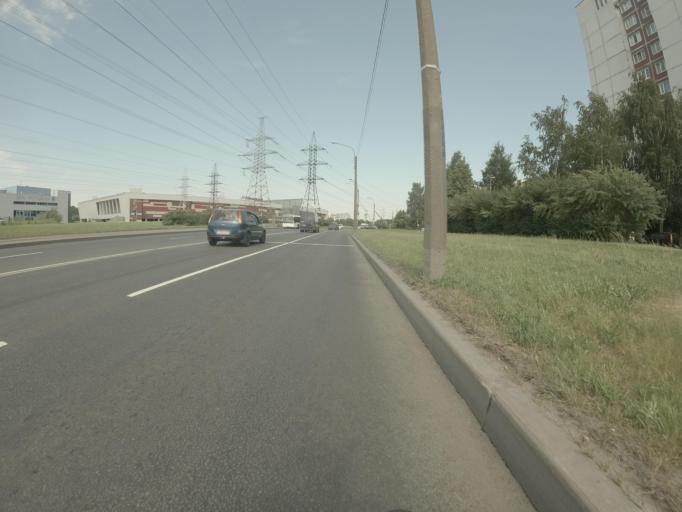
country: RU
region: St.-Petersburg
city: Krasnogvargeisky
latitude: 59.9453
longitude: 30.4619
